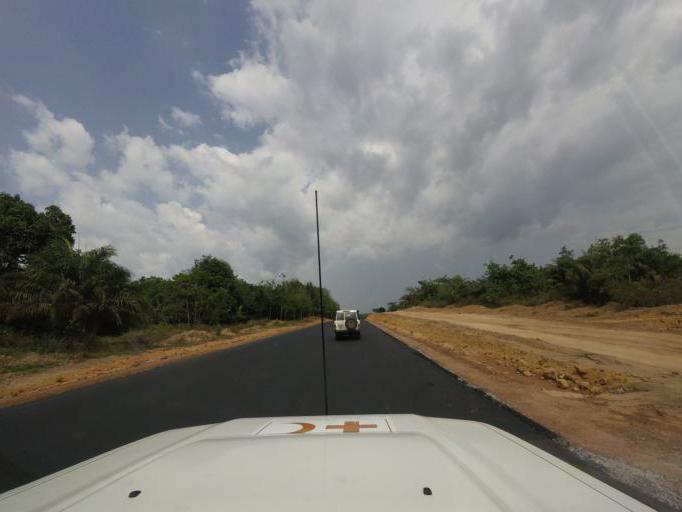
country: LR
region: Margibi
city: Kakata
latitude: 6.7274
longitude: -10.1426
